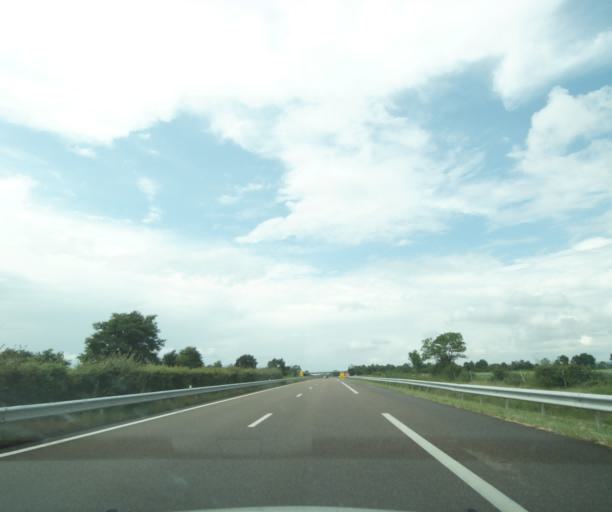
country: FR
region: Auvergne
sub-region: Departement de l'Allier
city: Estivareilles
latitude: 46.4544
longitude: 2.6866
